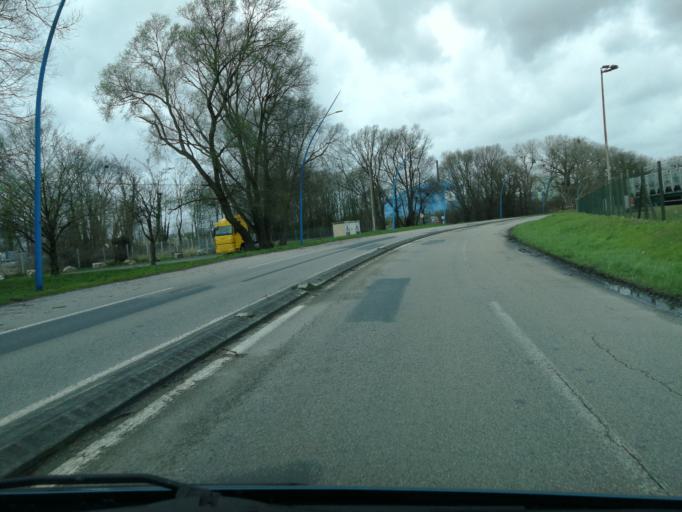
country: FR
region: Haute-Normandie
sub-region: Departement de l'Eure
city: Quillebeuf-sur-Seine
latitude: 49.4767
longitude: 0.5327
